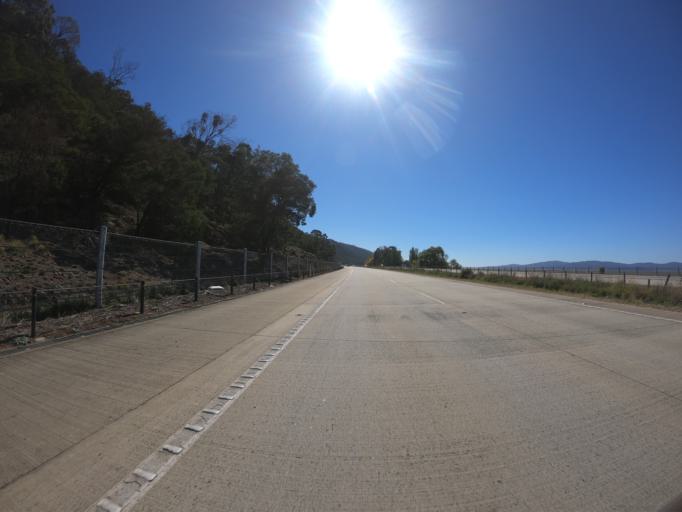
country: AU
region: New South Wales
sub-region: Yass Valley
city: Gundaroo
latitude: -35.0756
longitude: 149.3744
